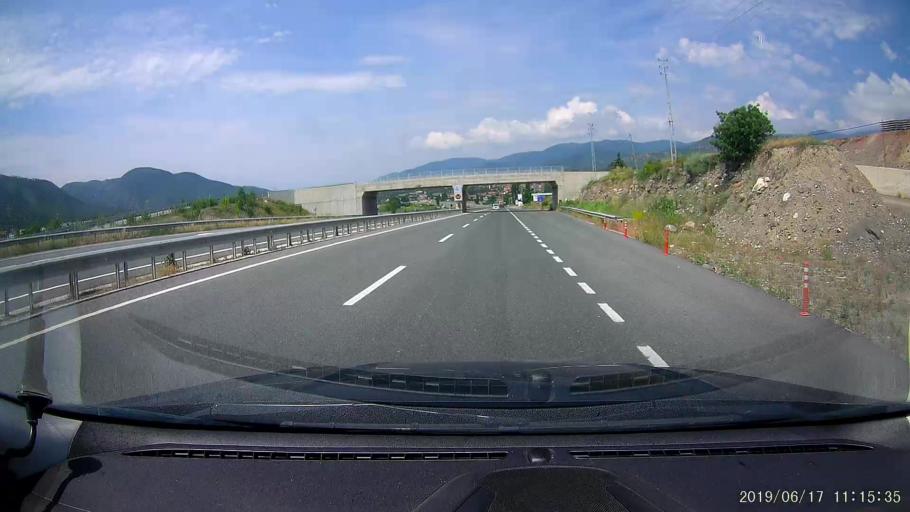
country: TR
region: Kastamonu
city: Tosya
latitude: 40.9509
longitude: 33.9208
